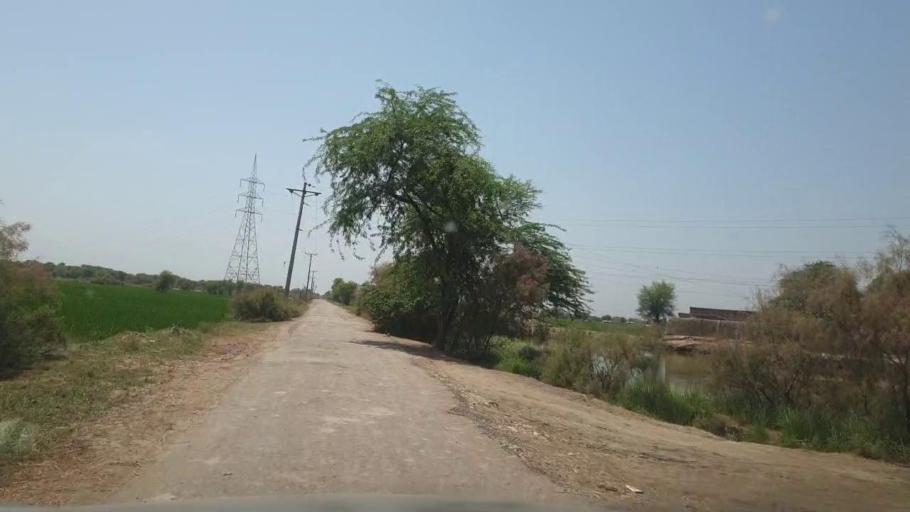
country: PK
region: Sindh
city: Warah
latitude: 27.4943
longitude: 67.7469
